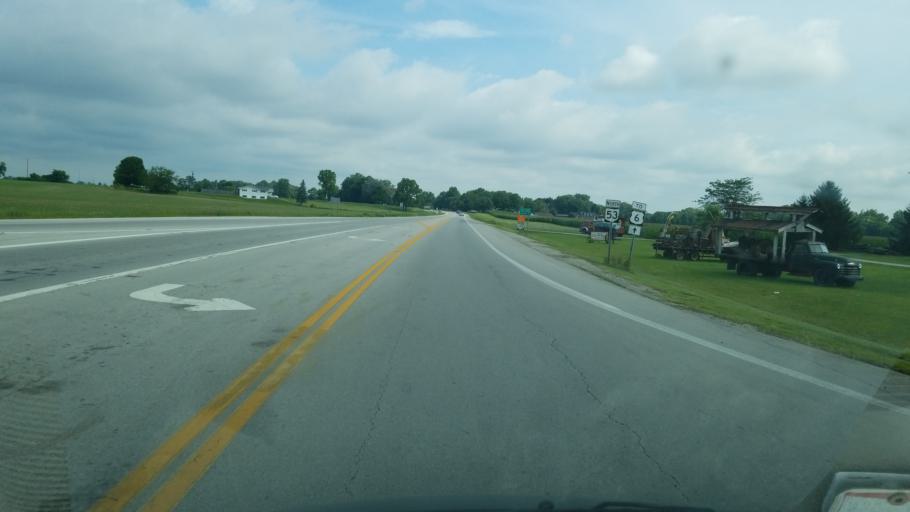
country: US
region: Ohio
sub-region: Sandusky County
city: Ballville
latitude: 41.2917
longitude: -83.1708
